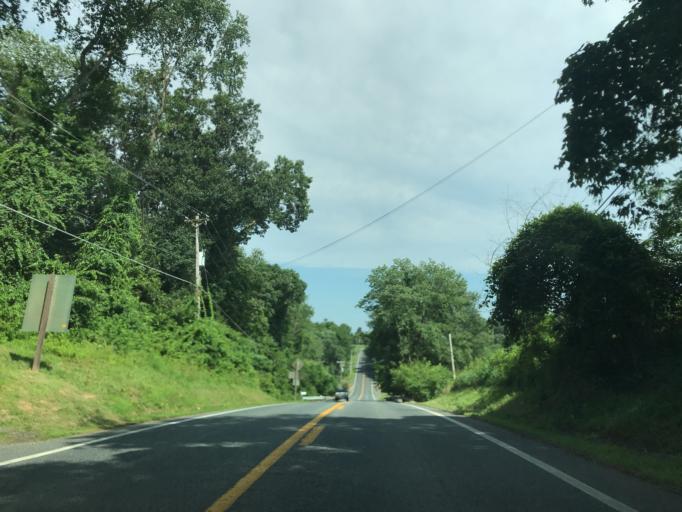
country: US
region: Pennsylvania
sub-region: York County
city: Susquehanna Trails
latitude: 39.6765
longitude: -76.3632
